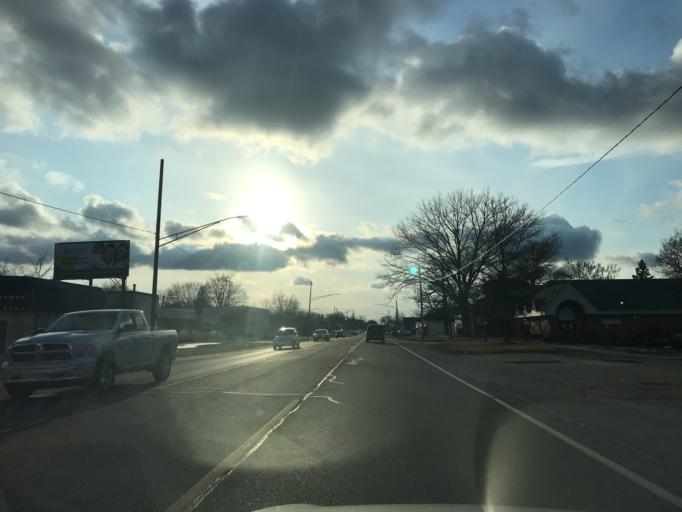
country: US
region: Michigan
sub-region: Wayne County
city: Redford
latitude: 42.4280
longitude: -83.3086
